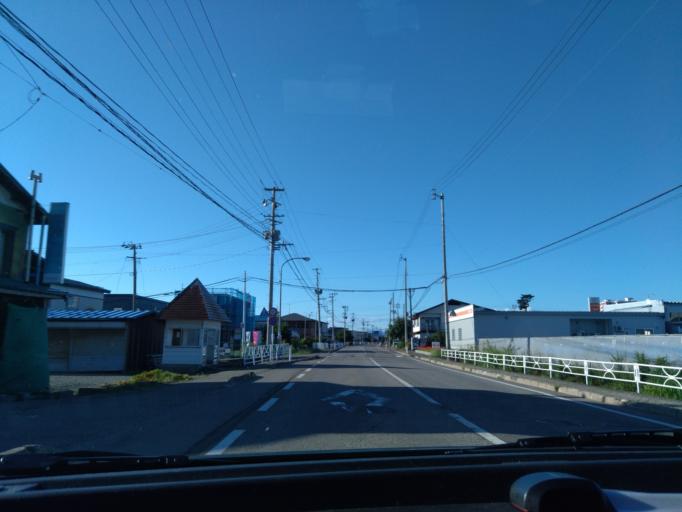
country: JP
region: Akita
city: Omagari
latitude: 39.4398
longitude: 140.4808
